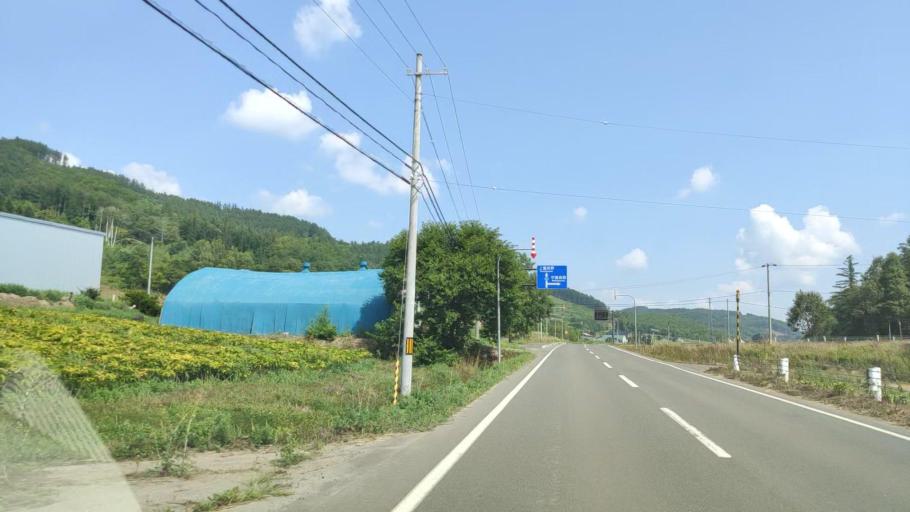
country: JP
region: Hokkaido
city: Shimo-furano
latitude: 43.4339
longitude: 142.4096
